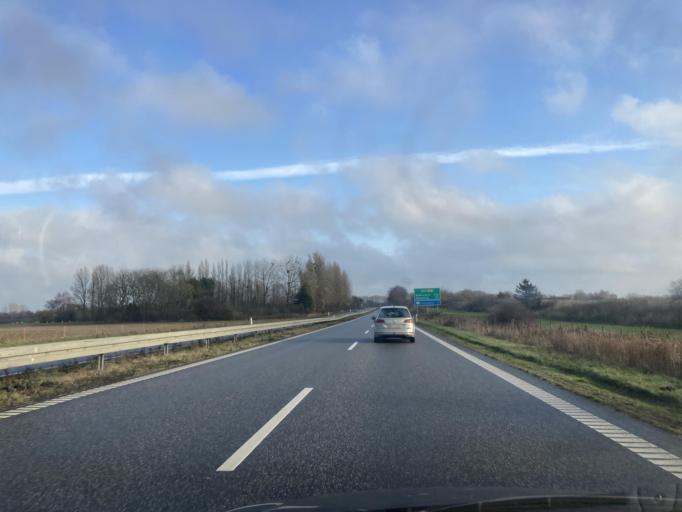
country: DK
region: Zealand
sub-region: Lolland Kommune
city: Maribo
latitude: 54.7856
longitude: 11.5065
